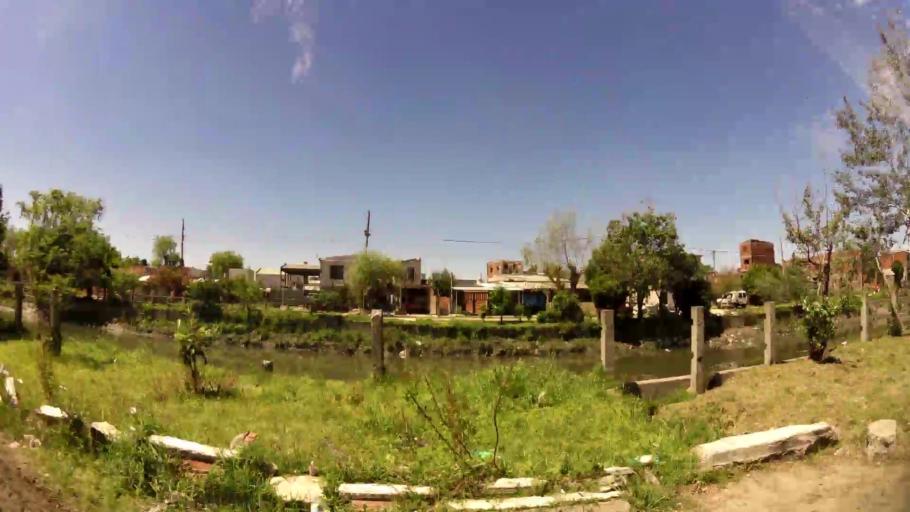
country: AR
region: Buenos Aires
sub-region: Partido de Quilmes
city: Quilmes
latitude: -34.7301
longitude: -58.3128
